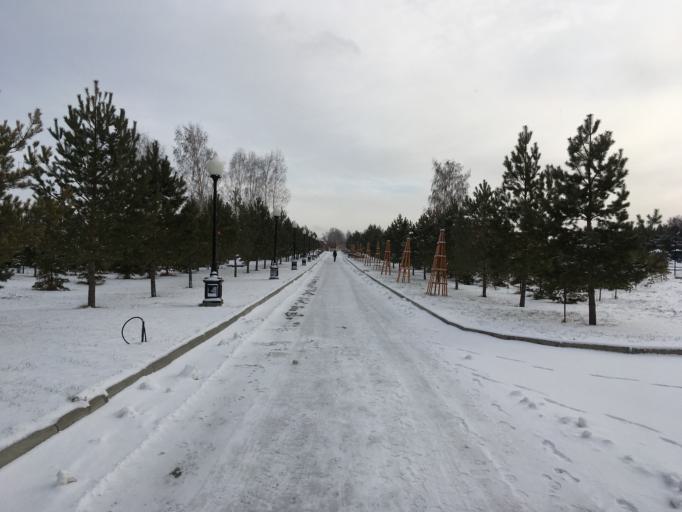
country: RU
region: Novosibirsk
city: Mochishche
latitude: 55.0766
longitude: 83.0604
